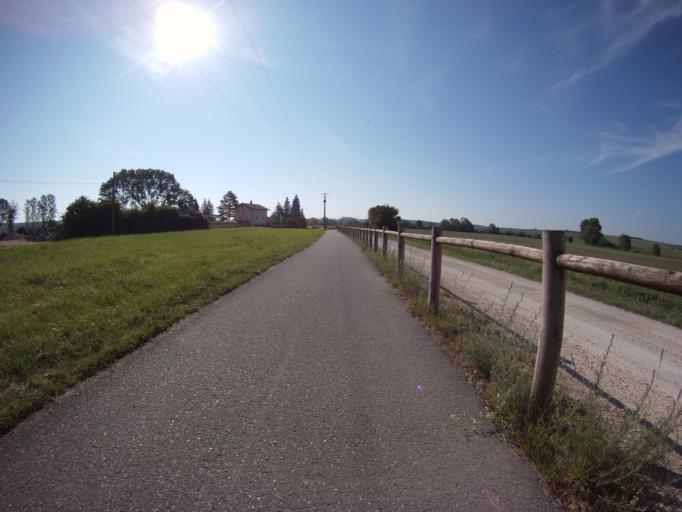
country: FR
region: Lorraine
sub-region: Departement de Meurthe-et-Moselle
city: Bouxieres-aux-Chenes
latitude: 48.7420
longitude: 6.2860
